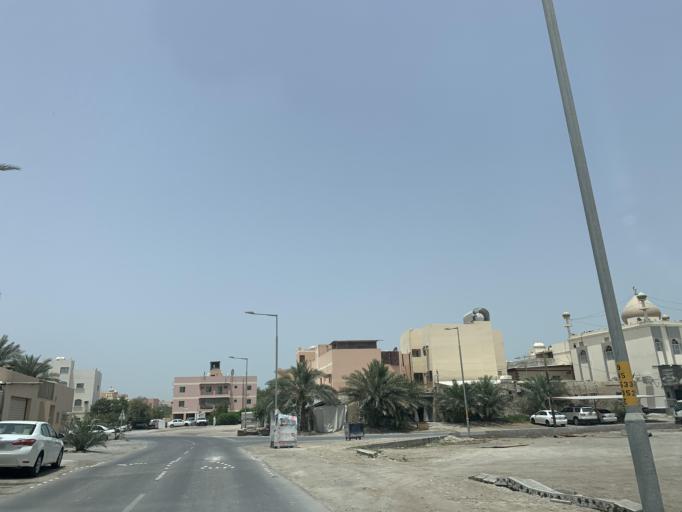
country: BH
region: Northern
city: Sitrah
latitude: 26.1495
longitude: 50.5863
